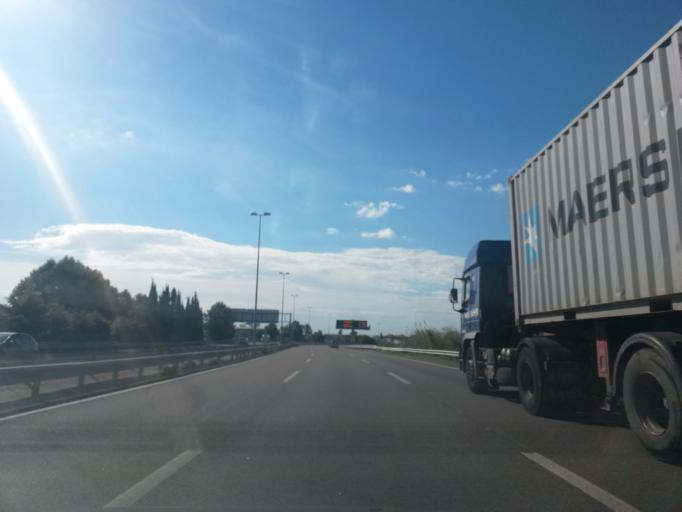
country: ES
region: Catalonia
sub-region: Provincia de Barcelona
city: Argentona
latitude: 41.5390
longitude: 2.4150
